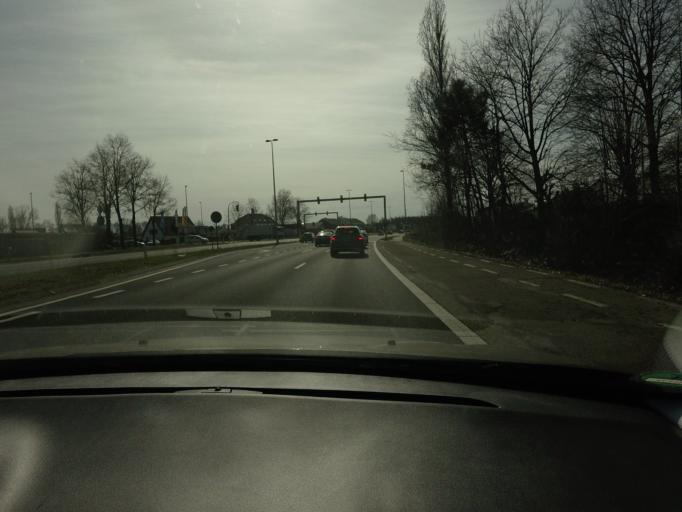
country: BE
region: Flanders
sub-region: Provincie Limburg
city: Zonhoven
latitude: 50.9760
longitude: 5.3626
